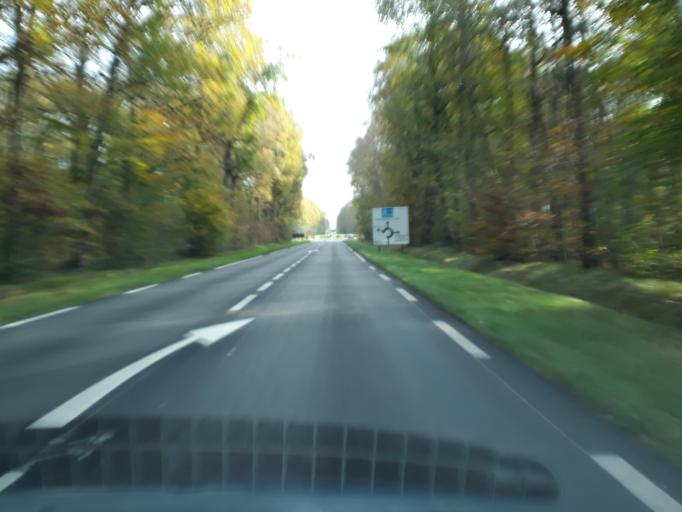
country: FR
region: Ile-de-France
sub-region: Departement de Seine-et-Marne
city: Thomery
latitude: 48.4208
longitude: 2.7879
